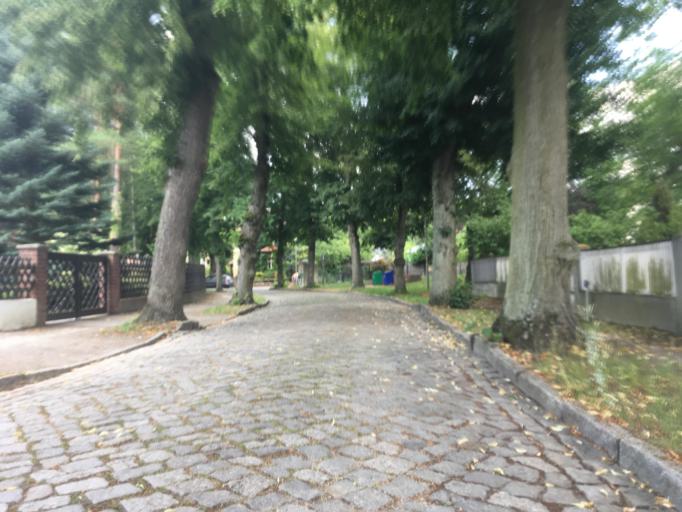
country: DE
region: Brandenburg
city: Wildau
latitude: 52.3420
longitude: 13.6278
